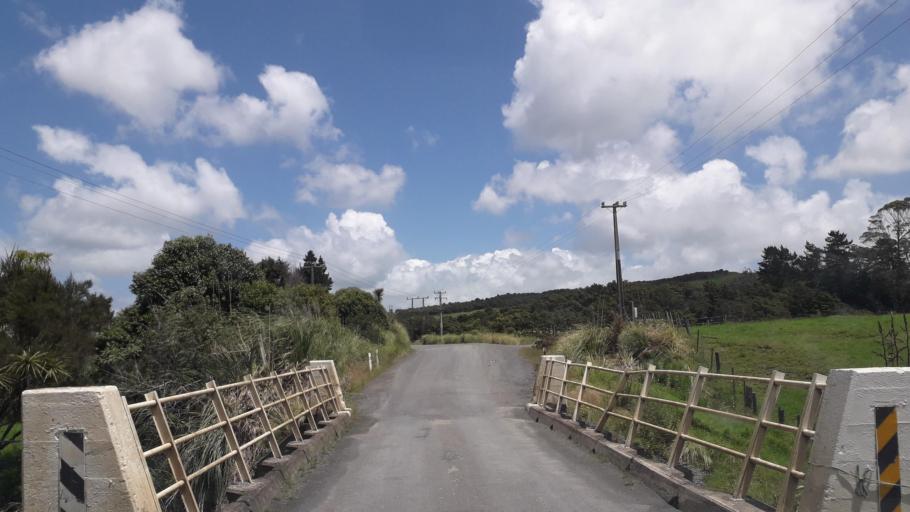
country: NZ
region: Northland
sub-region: Far North District
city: Taipa
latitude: -35.0135
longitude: 173.4196
